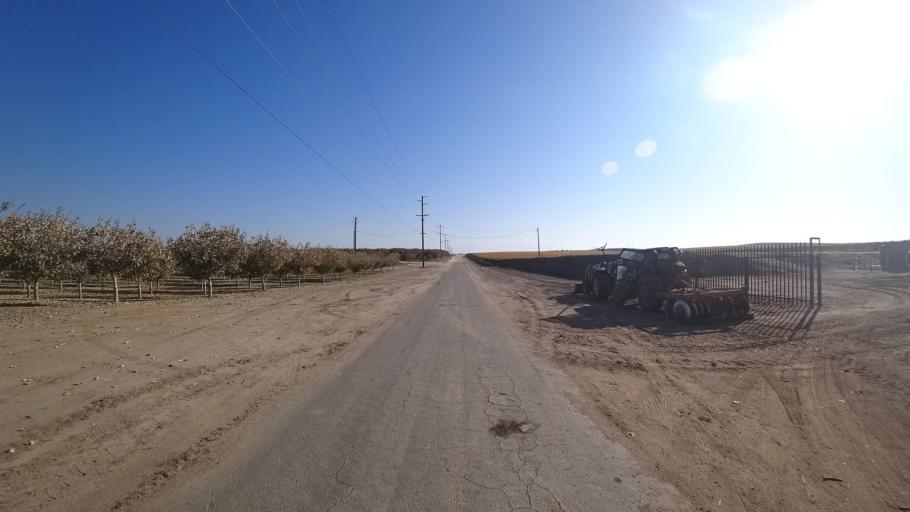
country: US
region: California
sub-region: Tulare County
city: Richgrove
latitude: 35.7328
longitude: -119.1065
